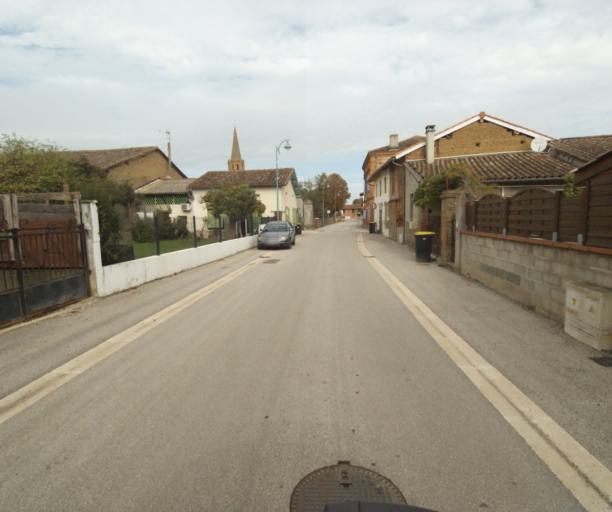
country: FR
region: Midi-Pyrenees
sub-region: Departement du Tarn-et-Garonne
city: Finhan
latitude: 43.9115
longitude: 1.2211
